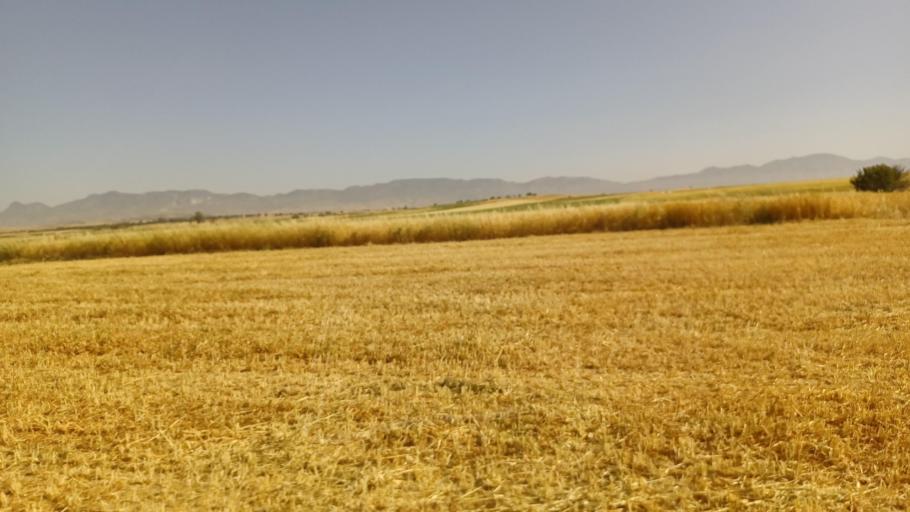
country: CY
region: Lefkosia
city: Mammari
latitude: 35.1669
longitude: 33.2398
